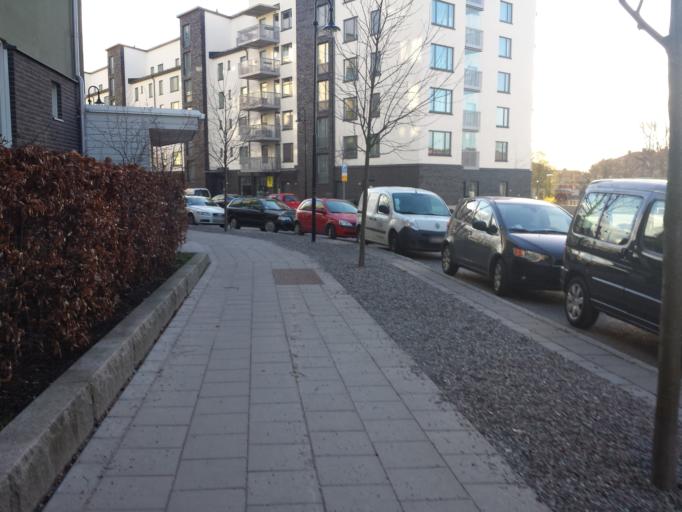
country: SE
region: Stockholm
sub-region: Solna Kommun
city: Solna
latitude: 59.3749
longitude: 18.0118
